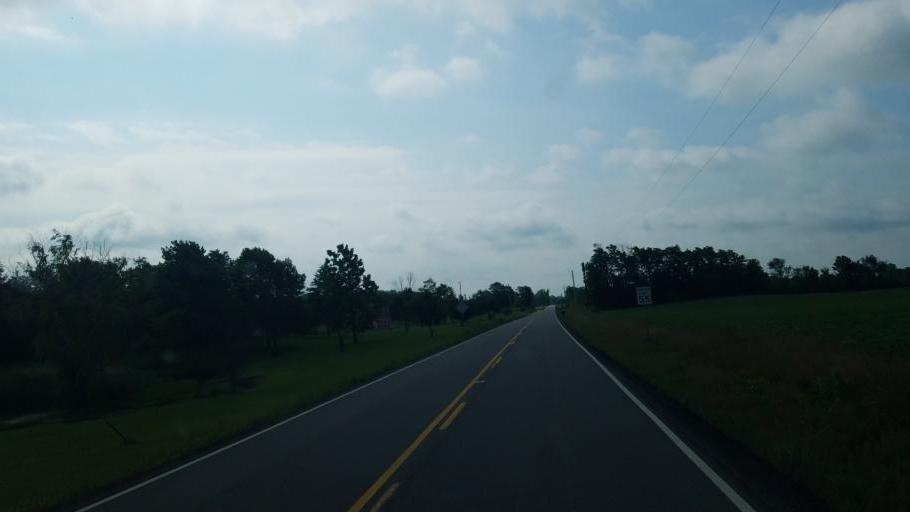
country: US
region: Ohio
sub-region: Knox County
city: Centerburg
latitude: 40.3169
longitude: -82.6611
